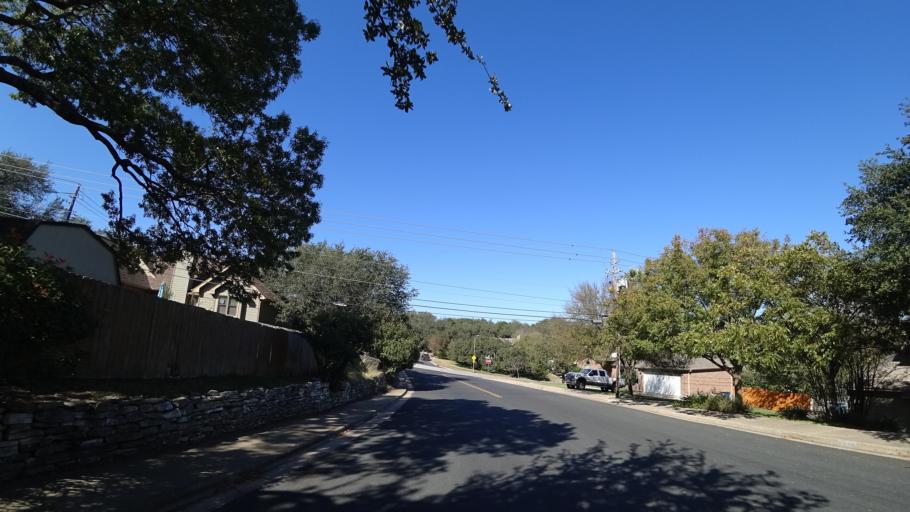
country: US
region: Texas
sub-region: Williamson County
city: Jollyville
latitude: 30.4189
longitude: -97.7637
